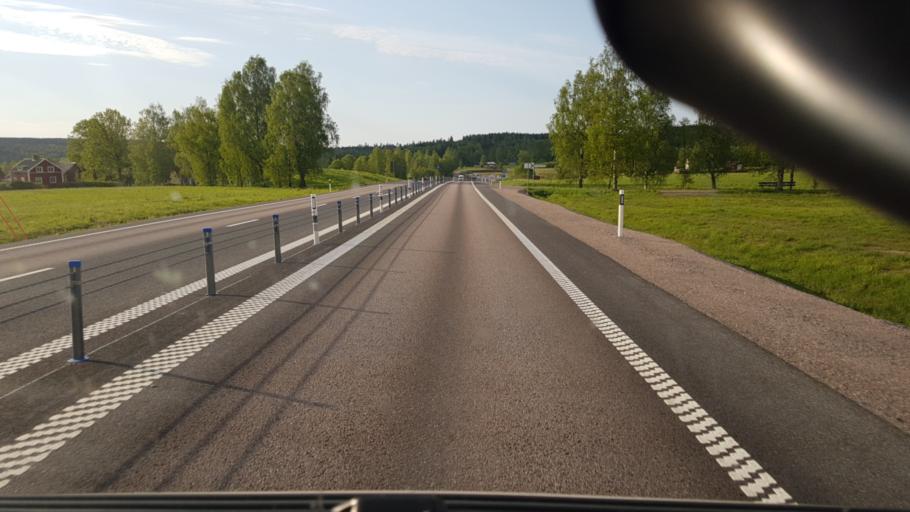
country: SE
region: Vaermland
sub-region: Eda Kommun
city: Amotfors
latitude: 59.7937
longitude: 12.3378
